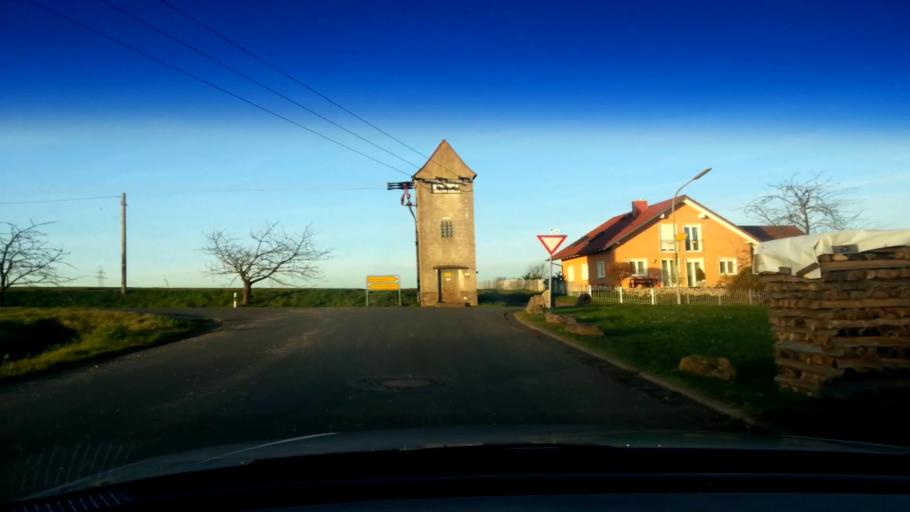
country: DE
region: Bavaria
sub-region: Upper Franconia
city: Rattelsdorf
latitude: 50.0675
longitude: 10.9003
